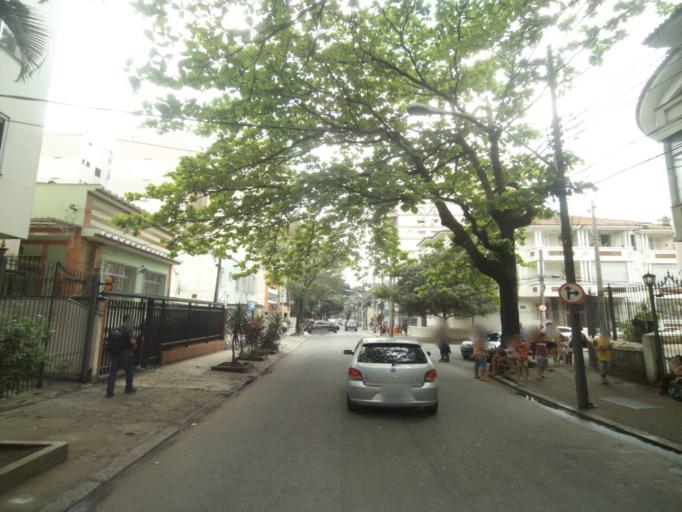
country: BR
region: Rio de Janeiro
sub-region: Rio De Janeiro
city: Rio de Janeiro
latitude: -22.9336
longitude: -43.2453
